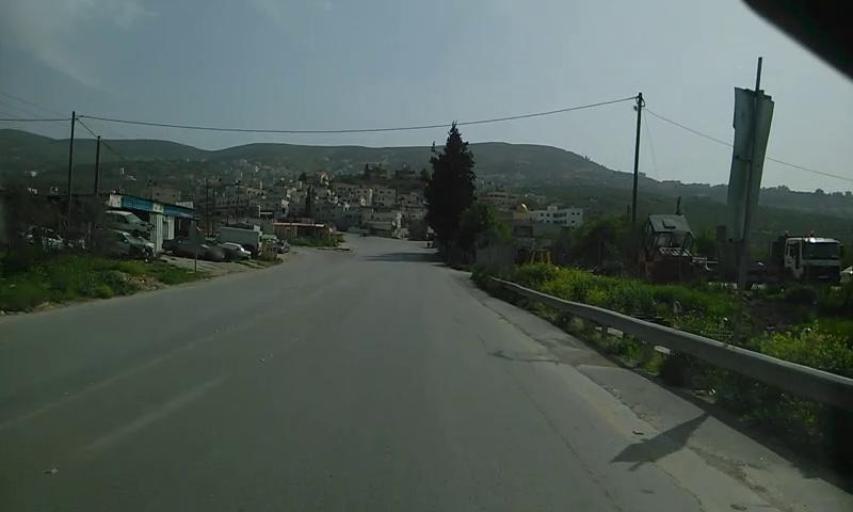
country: PS
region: West Bank
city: Al Fandaqumiyah
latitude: 32.3330
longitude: 35.2047
